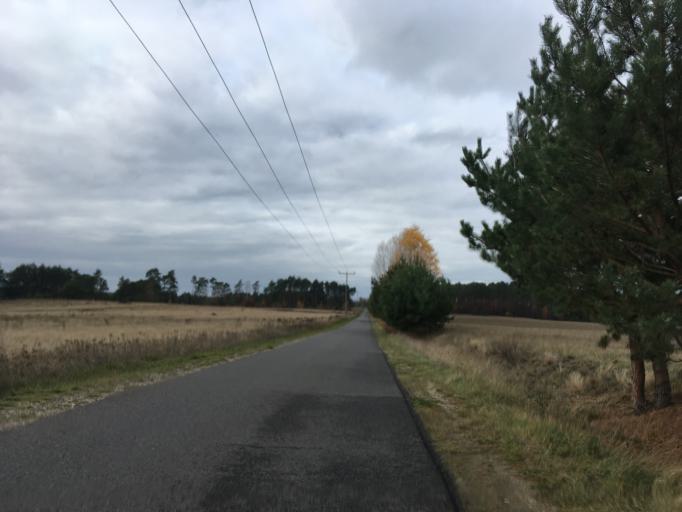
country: DE
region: Brandenburg
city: Jamlitz
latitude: 52.0823
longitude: 14.4480
